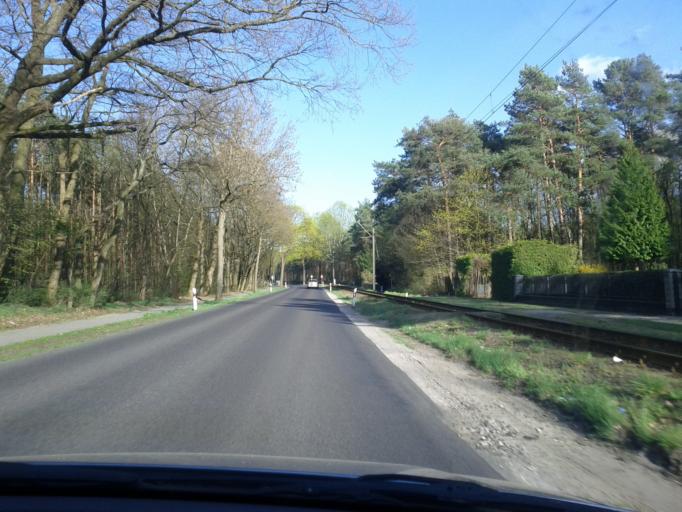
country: DE
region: Brandenburg
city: Woltersdorf
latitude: 52.4723
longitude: 13.7387
